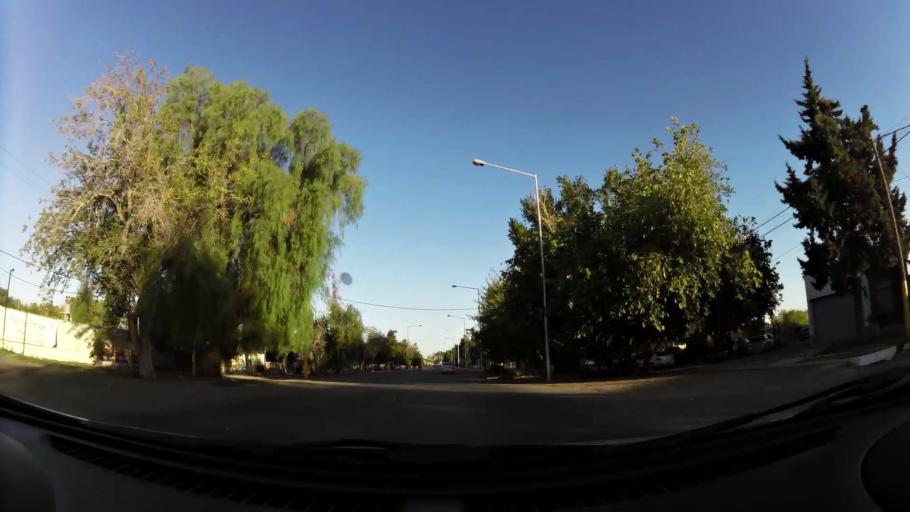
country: AR
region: San Juan
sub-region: Departamento de Santa Lucia
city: Santa Lucia
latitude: -31.5431
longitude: -68.4923
